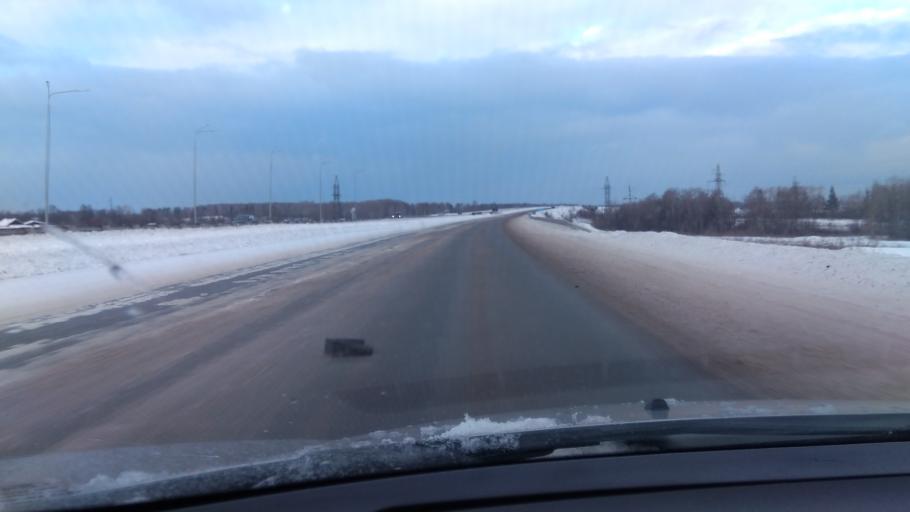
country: RU
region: Sverdlovsk
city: Tsementnyy
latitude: 57.4981
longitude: 60.1746
